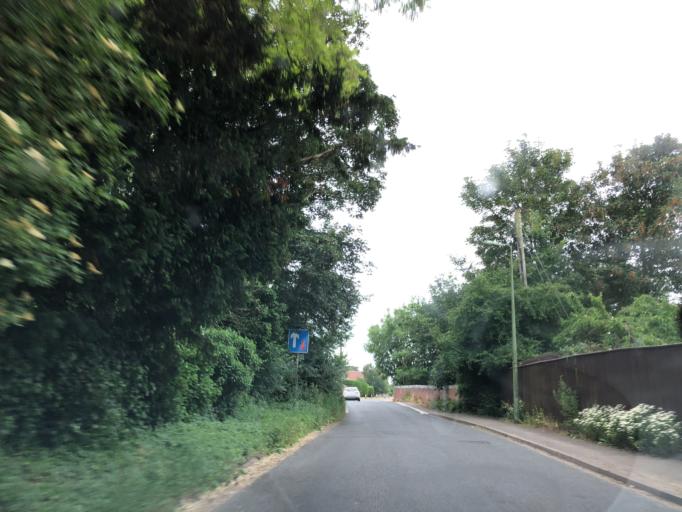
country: GB
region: England
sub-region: Suffolk
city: Thurston
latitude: 52.2503
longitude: 0.8145
